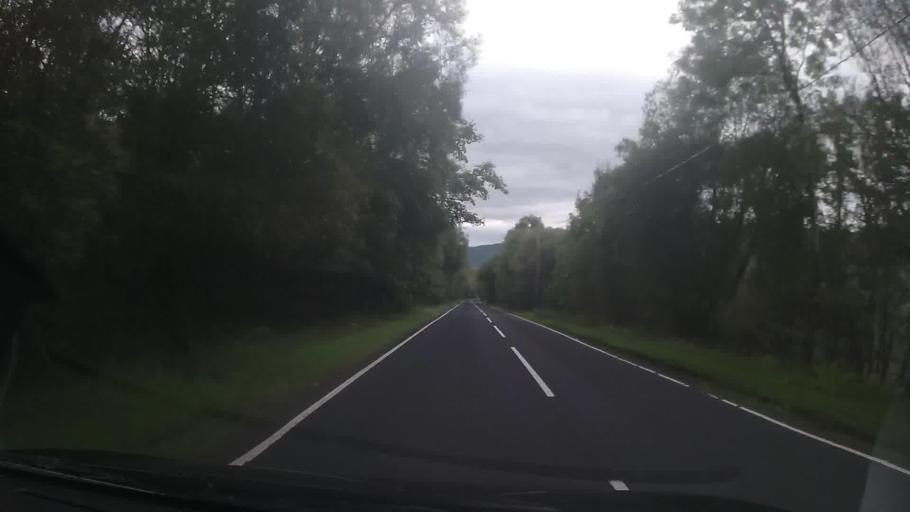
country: GB
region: Scotland
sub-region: Argyll and Bute
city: Garelochhead
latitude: 56.2261
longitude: -4.9887
